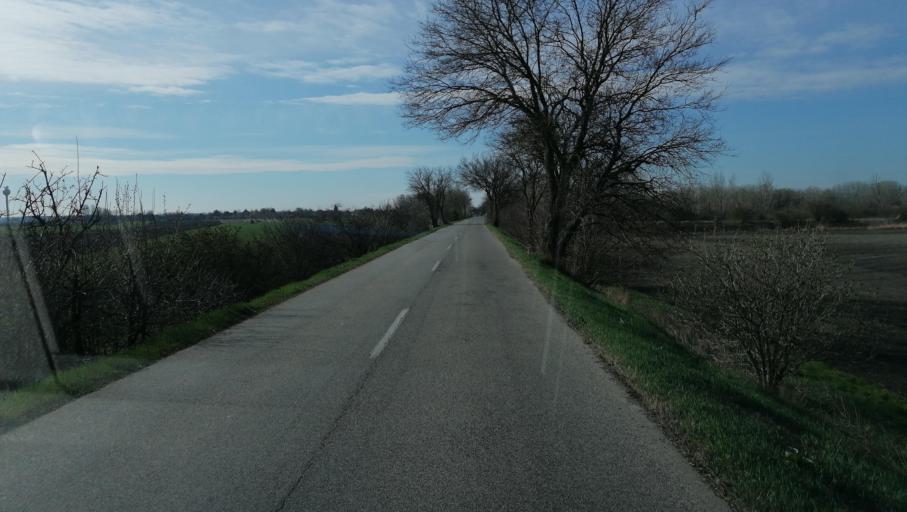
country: HU
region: Pest
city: Rackeve
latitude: 47.1013
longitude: 18.9269
